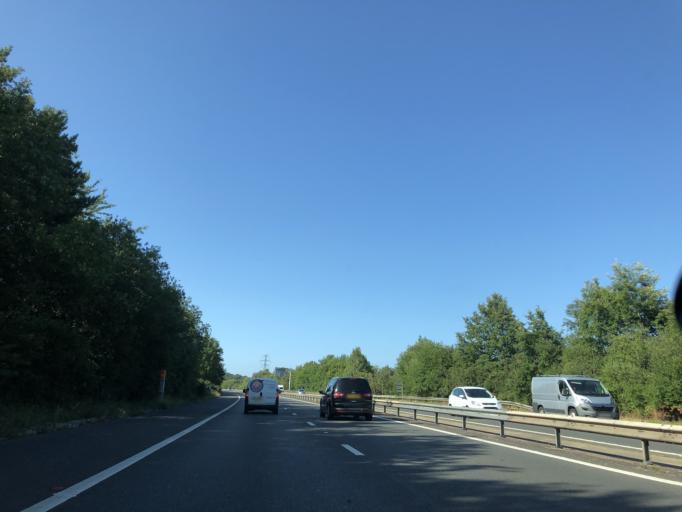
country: GB
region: England
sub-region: Hampshire
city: Cowplain
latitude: 50.8946
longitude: -0.9994
